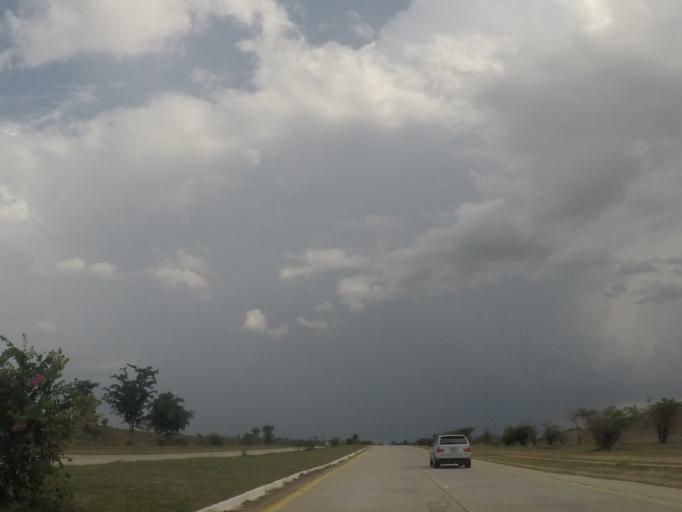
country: MM
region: Mandalay
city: Meiktila
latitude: 21.0938
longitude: 95.7937
